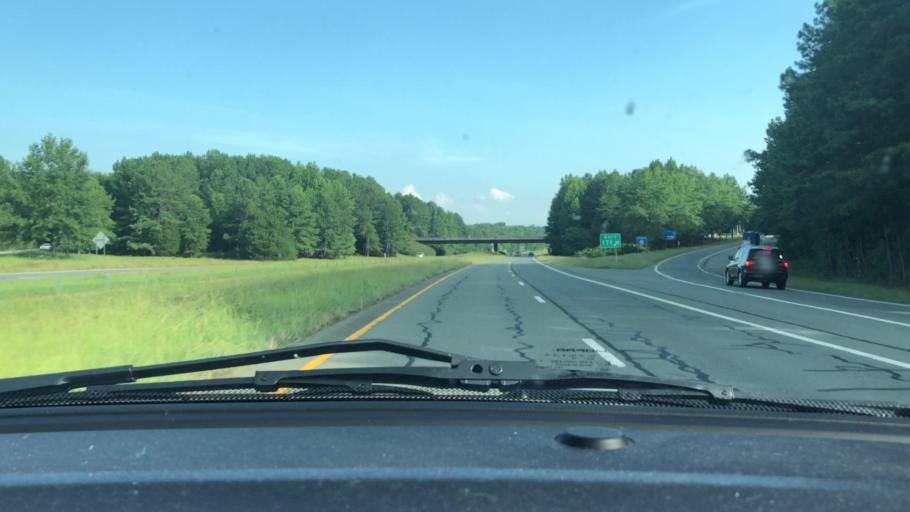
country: US
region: North Carolina
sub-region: Chatham County
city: Siler City
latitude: 35.7372
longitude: -79.4331
